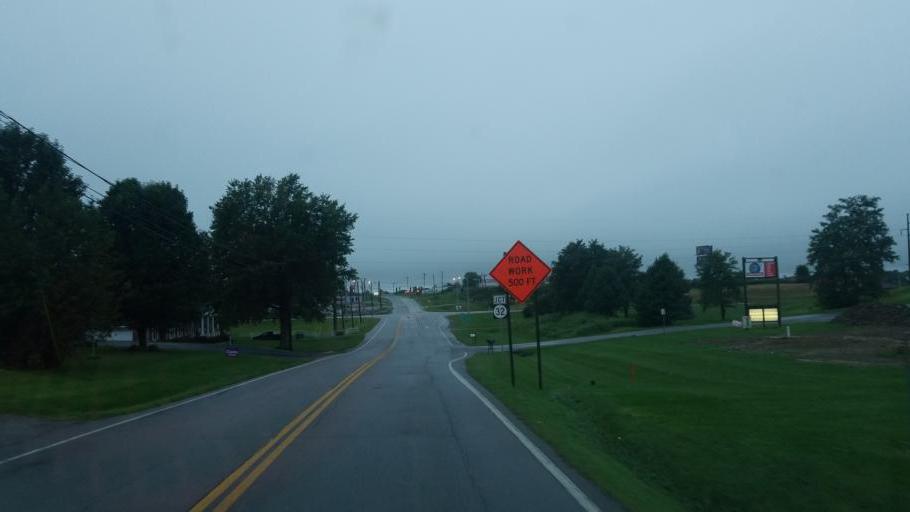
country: US
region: Kentucky
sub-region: Fleming County
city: Flemingsburg
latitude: 38.4146
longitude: -83.7382
